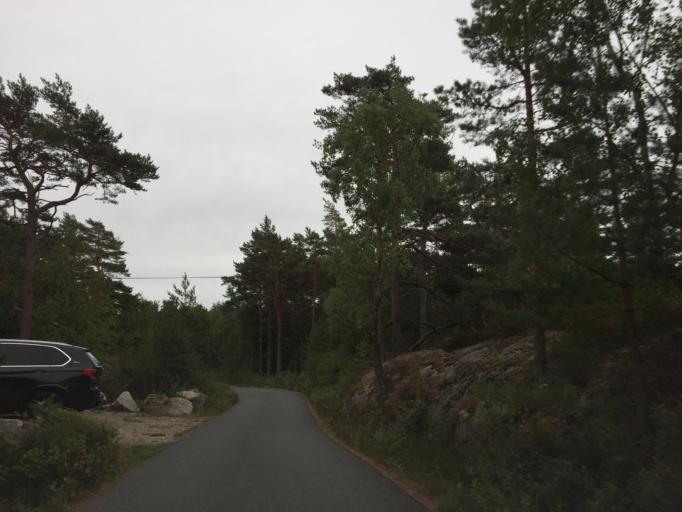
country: NO
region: Ostfold
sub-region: Hvaler
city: Skjaerhalden
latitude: 59.0809
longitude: 11.0012
